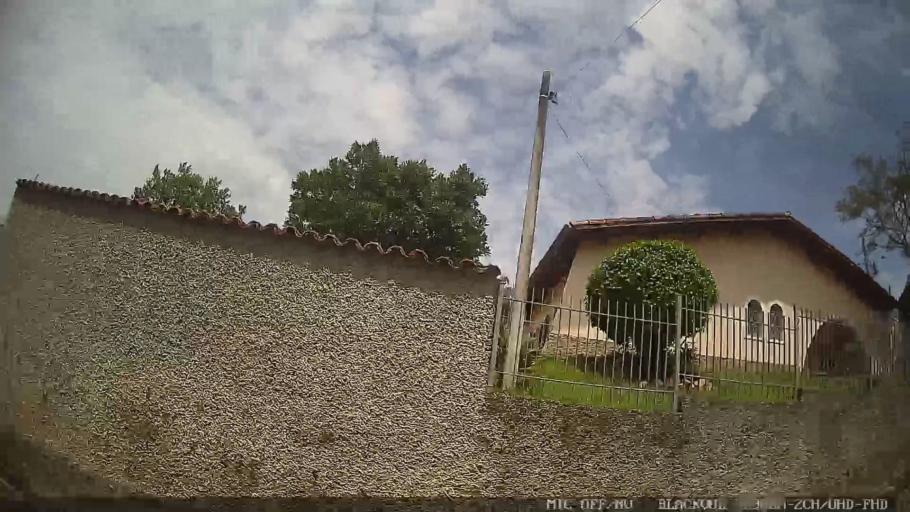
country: BR
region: Sao Paulo
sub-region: Ribeirao Pires
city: Ribeirao Pires
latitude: -23.7174
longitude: -46.4256
